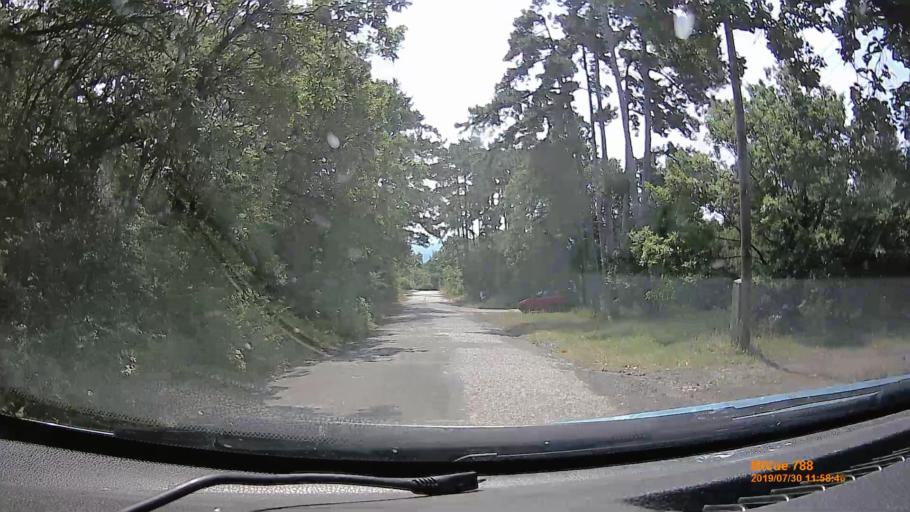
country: HU
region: Baranya
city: Pecs
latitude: 46.0907
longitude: 18.2148
